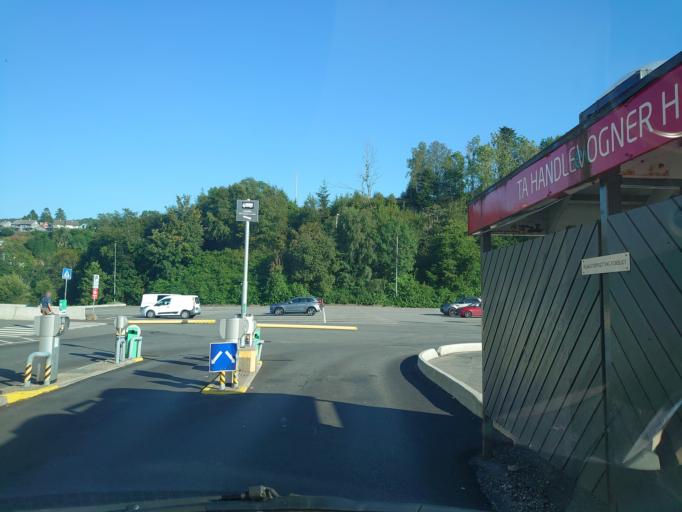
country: NO
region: Hordaland
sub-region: Bergen
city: Sandsli
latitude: 60.2961
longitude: 5.3303
